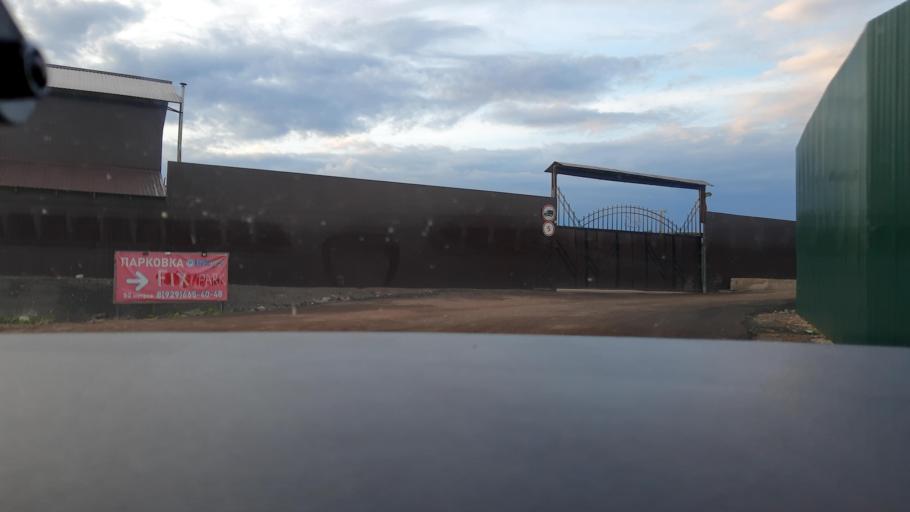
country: RU
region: Moskovskaya
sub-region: Leninskiy Rayon
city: Molokovo
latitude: 55.4782
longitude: 37.8556
